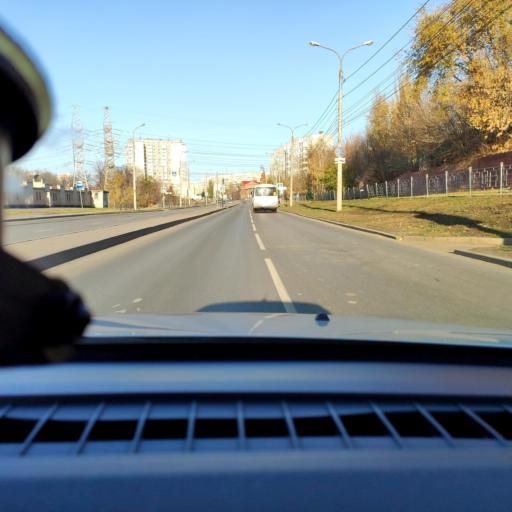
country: RU
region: Samara
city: Samara
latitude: 53.2463
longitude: 50.1948
